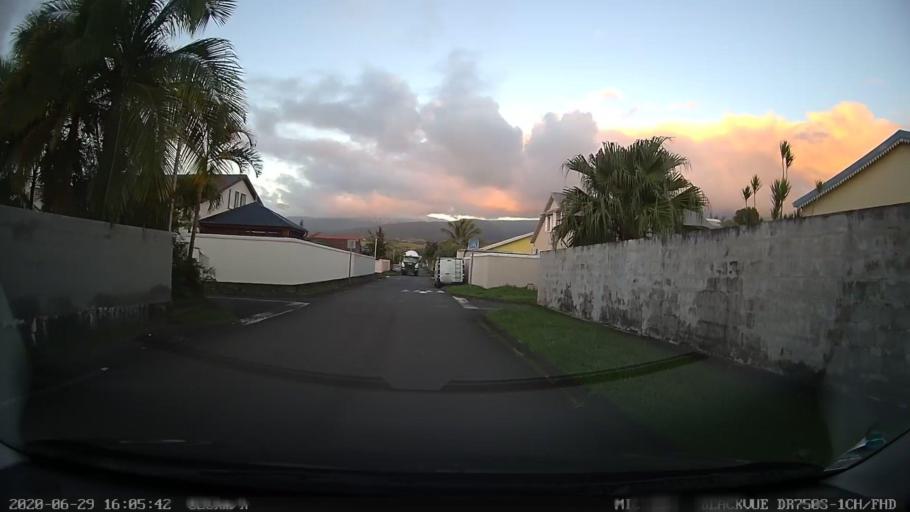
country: RE
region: Reunion
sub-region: Reunion
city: Bras-Panon
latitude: -20.9925
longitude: 55.6827
